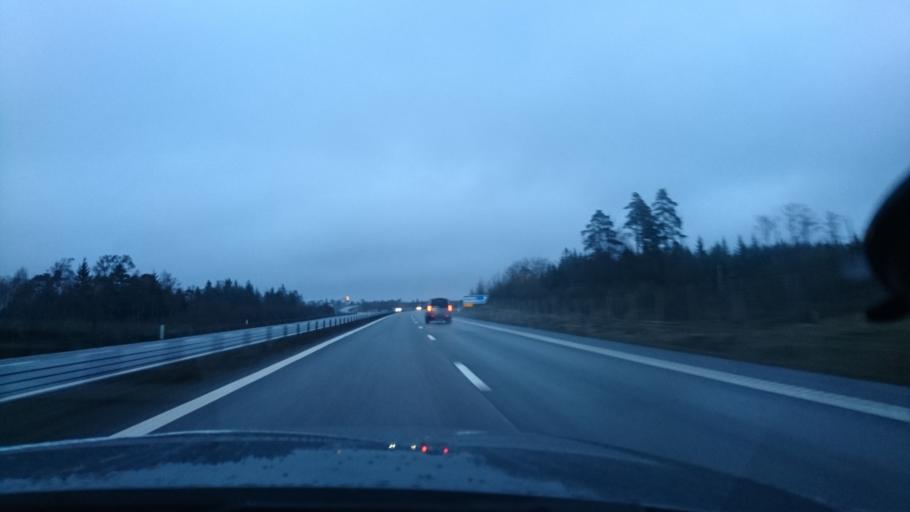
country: SE
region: Kronoberg
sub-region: Markaryds Kommun
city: Markaryd
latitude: 56.3557
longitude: 13.4718
